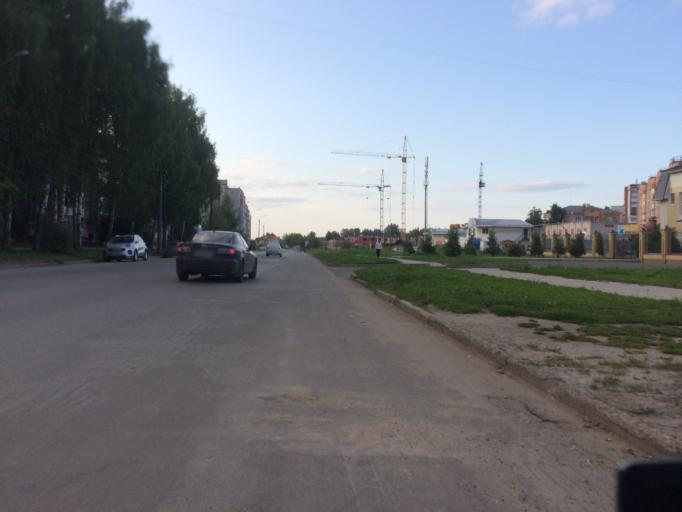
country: RU
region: Mariy-El
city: Medvedevo
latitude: 56.6427
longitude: 47.8449
